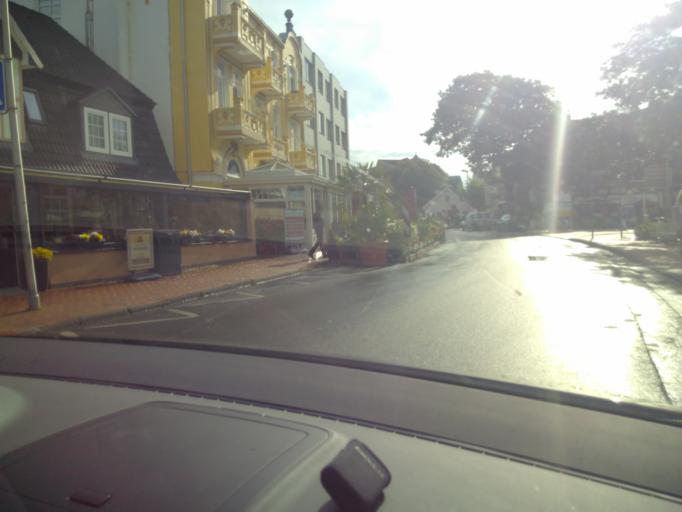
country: DE
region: Lower Saxony
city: Cuxhaven
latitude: 53.8852
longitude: 8.6422
